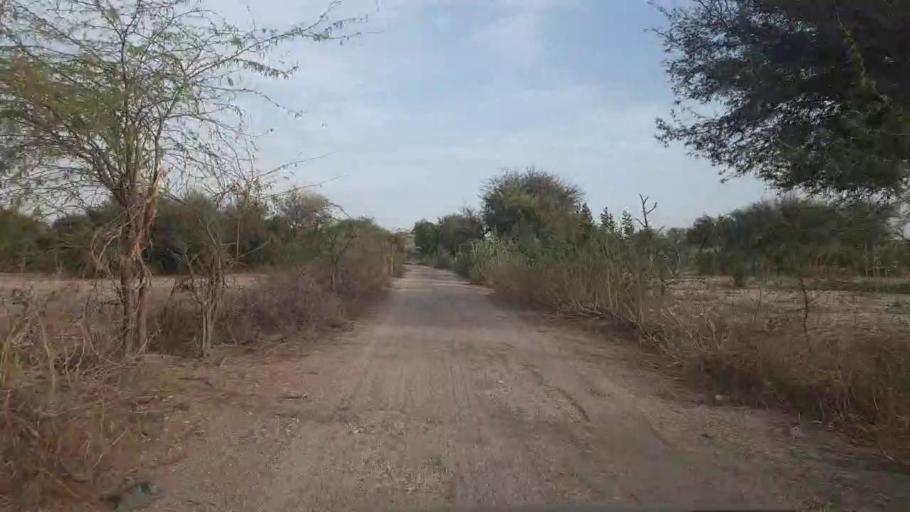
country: PK
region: Sindh
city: Nabisar
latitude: 25.1002
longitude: 69.6676
